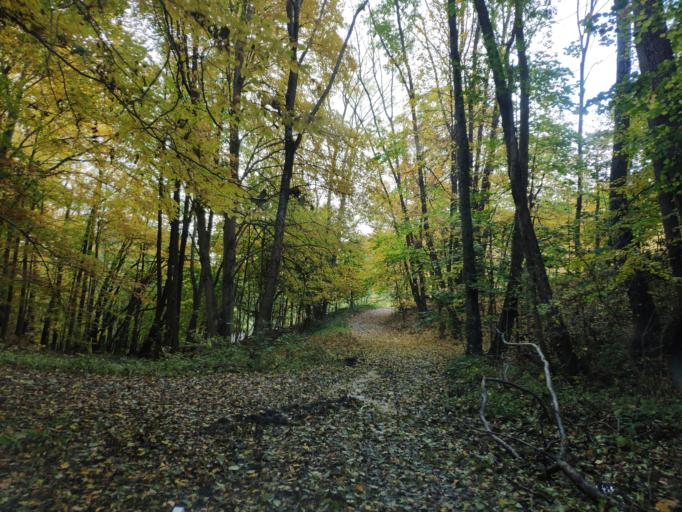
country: SK
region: Kosicky
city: Moldava nad Bodvou
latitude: 48.7200
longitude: 21.0107
